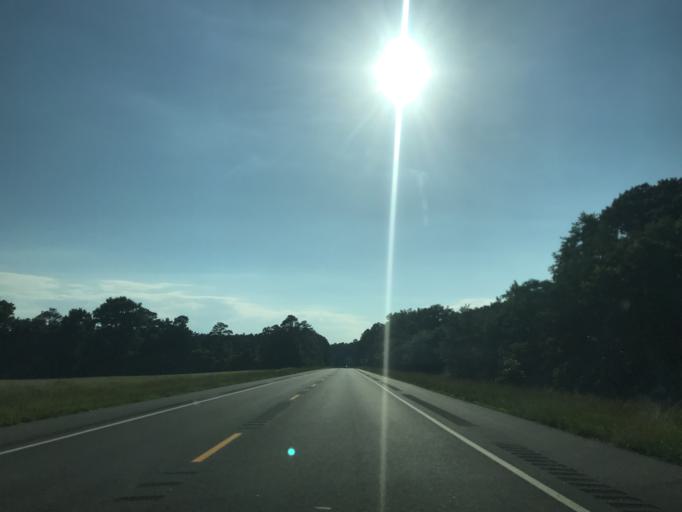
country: US
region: Maryland
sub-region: Wicomico County
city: Hebron
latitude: 38.5332
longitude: -75.7205
